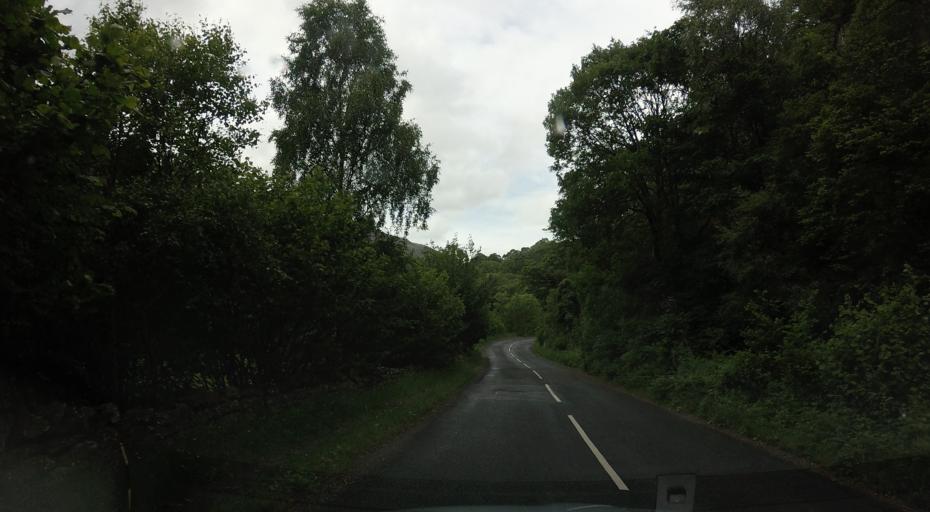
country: GB
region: England
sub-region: Cumbria
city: Keswick
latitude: 54.5348
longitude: -3.1538
